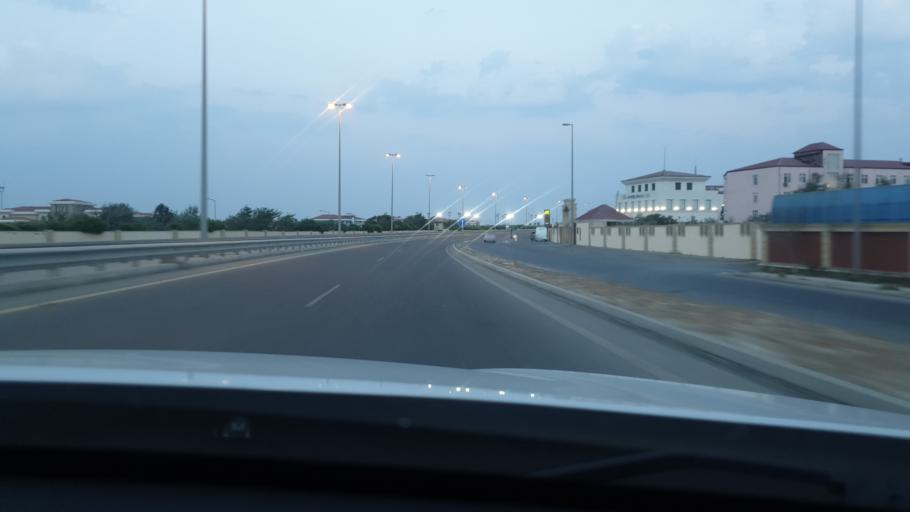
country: AZ
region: Baki
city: Bilajer
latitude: 40.5894
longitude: 50.0552
